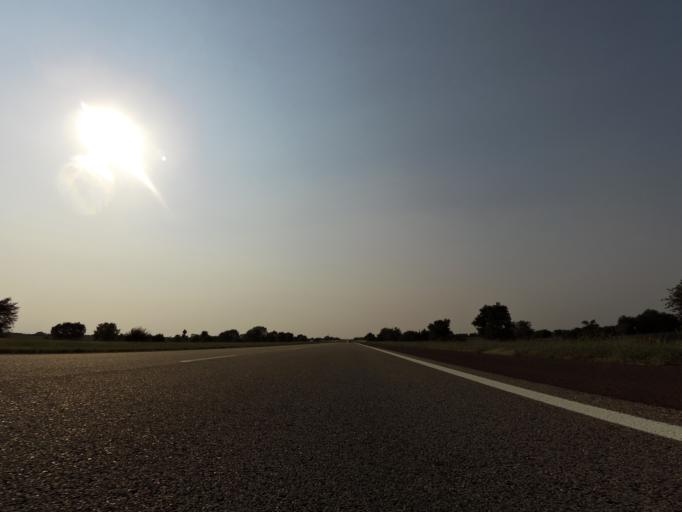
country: US
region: Kansas
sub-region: Reno County
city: Haven
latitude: 37.9212
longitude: -97.8316
